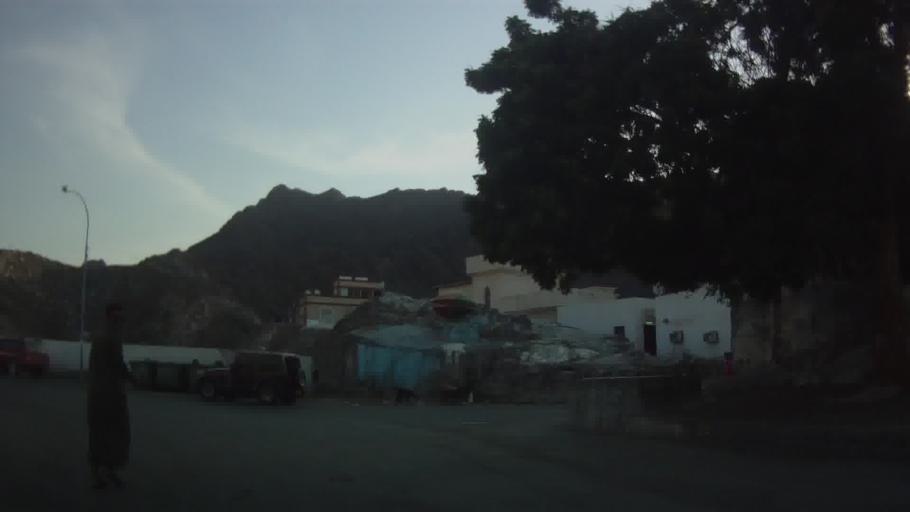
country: OM
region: Muhafazat Masqat
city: Muscat
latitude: 23.5936
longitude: 58.6028
